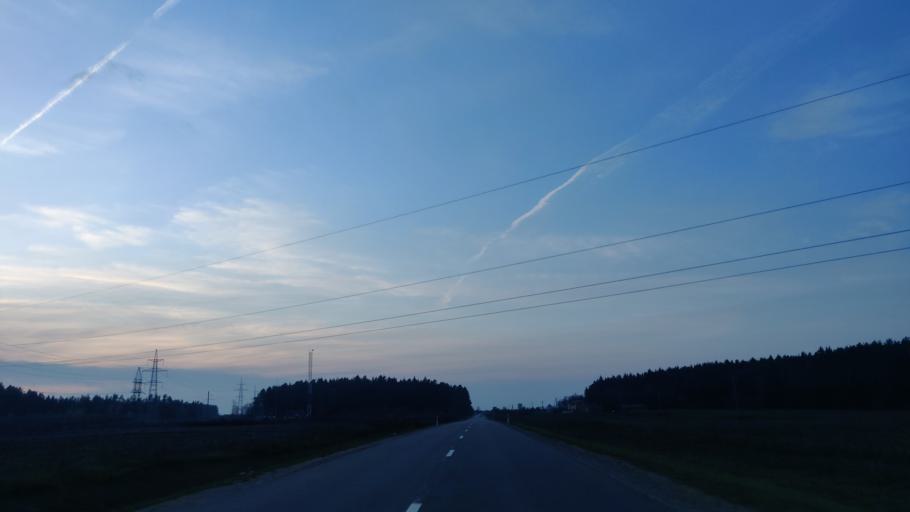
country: LT
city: Lentvaris
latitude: 54.5965
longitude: 25.0328
